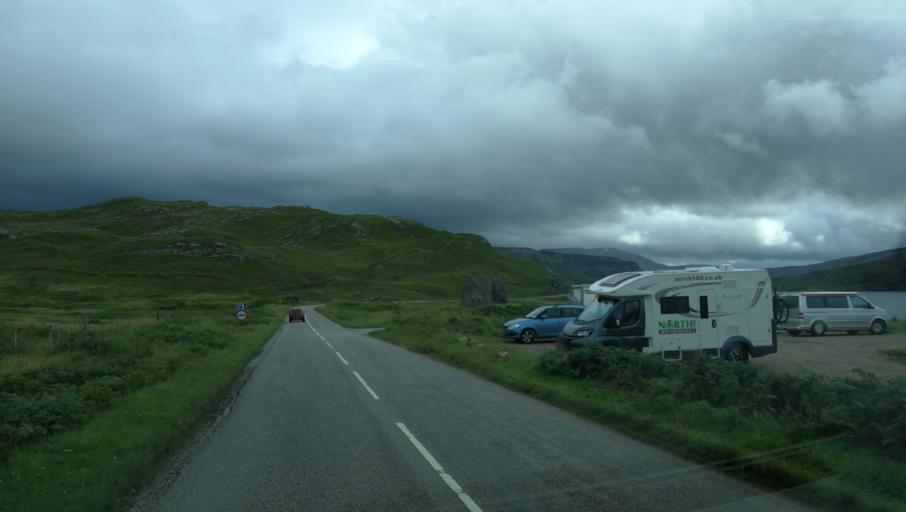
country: GB
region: Scotland
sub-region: Highland
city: Ullapool
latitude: 58.1662
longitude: -4.9888
